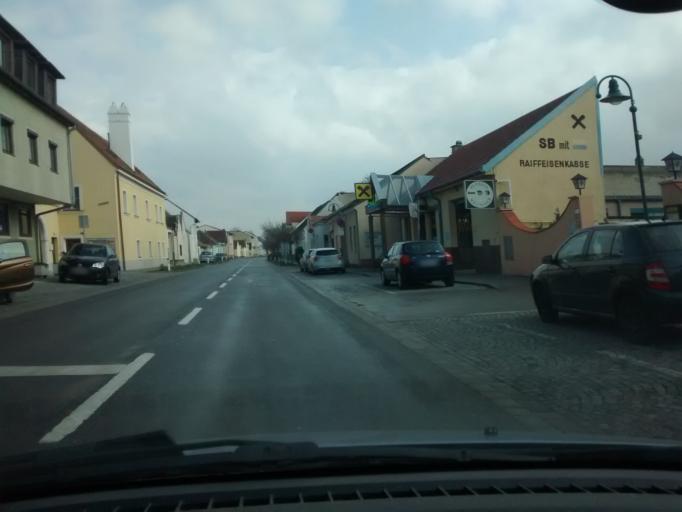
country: AT
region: Lower Austria
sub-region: Politischer Bezirk Modling
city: Munchendorf
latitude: 48.0284
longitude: 16.3794
